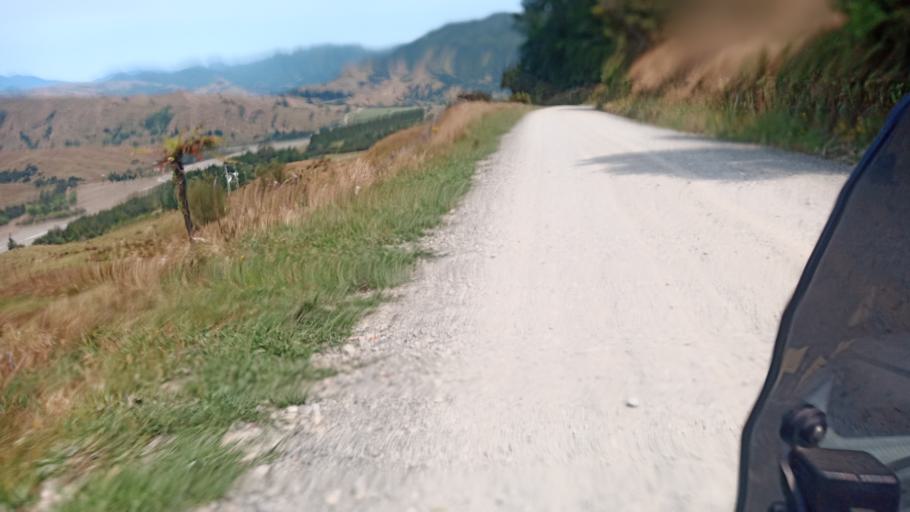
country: NZ
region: Bay of Plenty
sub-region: Opotiki District
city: Opotiki
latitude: -37.6577
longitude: 178.1273
